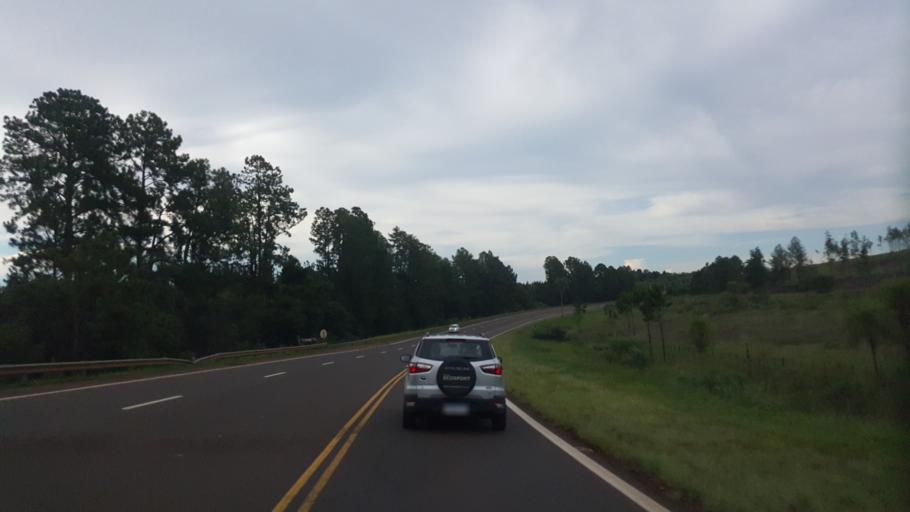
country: AR
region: Misiones
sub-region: Departamento de Candelaria
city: Loreto
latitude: -27.3237
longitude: -55.5452
